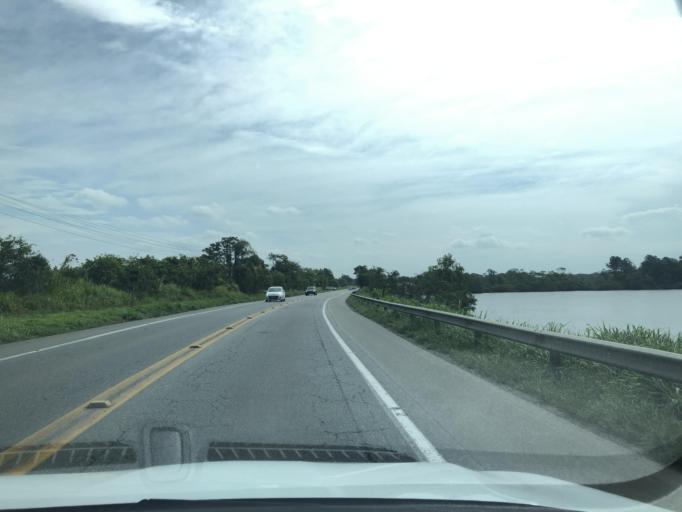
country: BR
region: Santa Catarina
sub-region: Sao Francisco Do Sul
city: Sao Francisco do Sul
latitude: -26.3672
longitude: -48.6667
